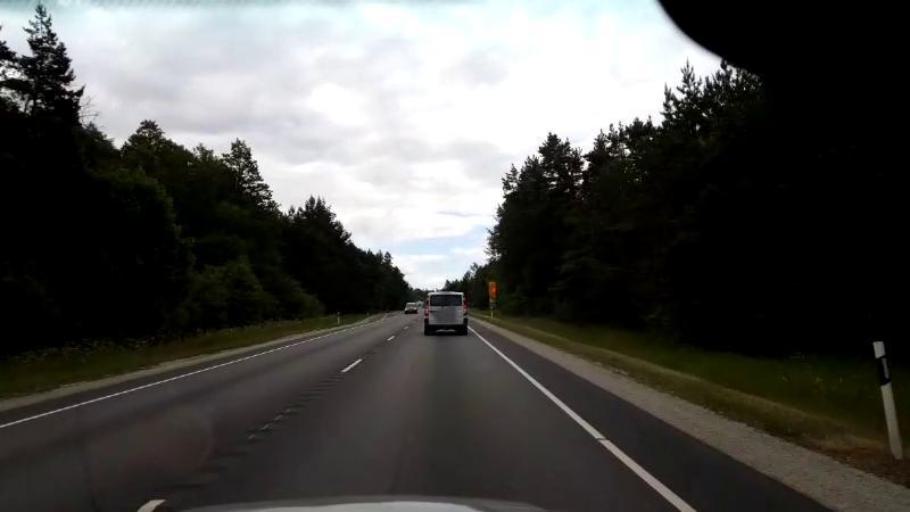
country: EE
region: Paernumaa
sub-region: Paernu linn
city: Parnu
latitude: 58.2092
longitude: 24.4852
